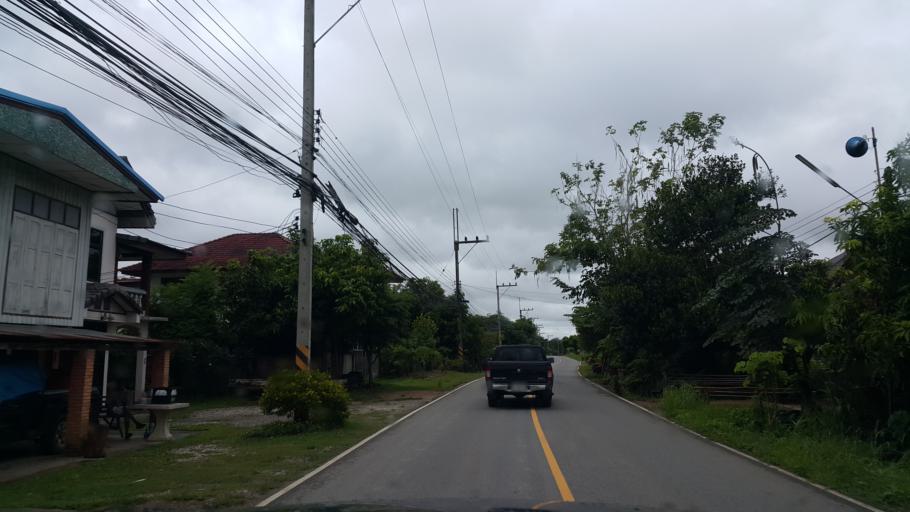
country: TH
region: Phayao
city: Chiang Kham
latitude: 19.5231
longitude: 100.3388
